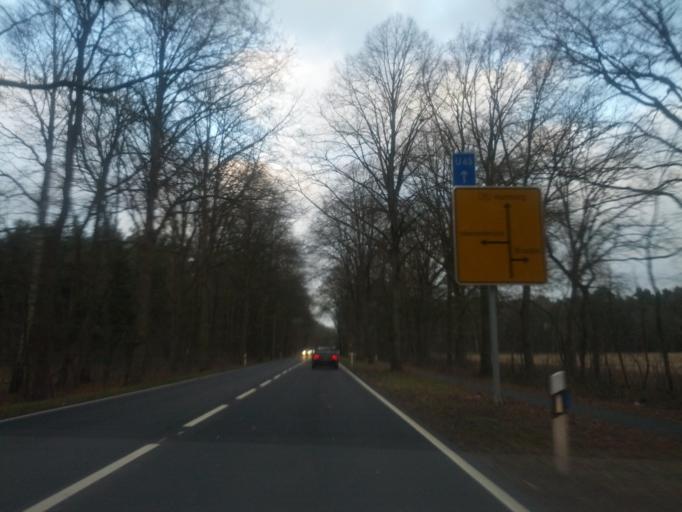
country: DE
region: Lower Saxony
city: Scheessel
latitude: 53.1452
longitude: 9.4592
